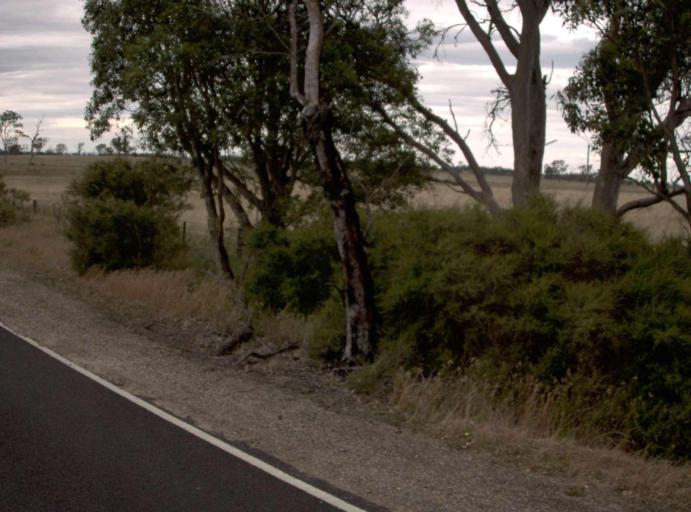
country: AU
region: Victoria
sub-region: Wellington
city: Sale
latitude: -38.0039
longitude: 147.1906
